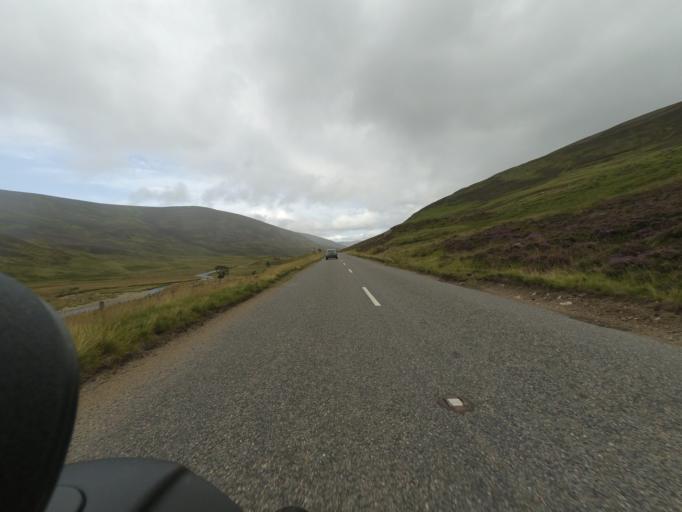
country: GB
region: Scotland
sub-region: Perth and Kinross
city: Blairgowrie
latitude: 56.9462
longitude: -3.4068
